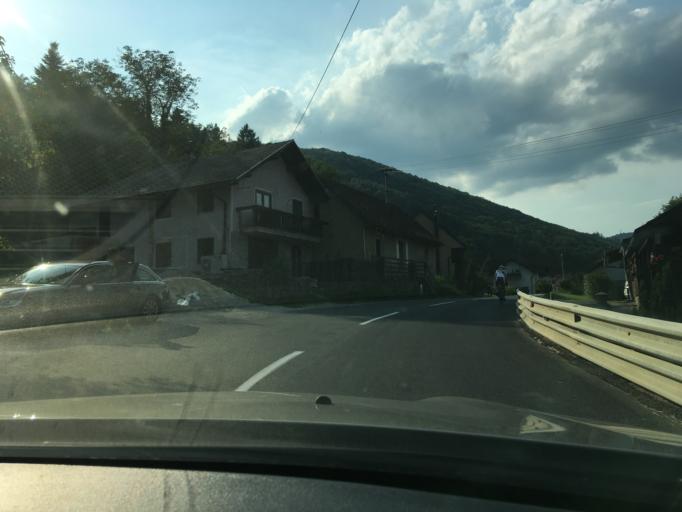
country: SI
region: Dolenjske Toplice
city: Dolenjske Toplice
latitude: 45.7611
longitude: 15.0301
